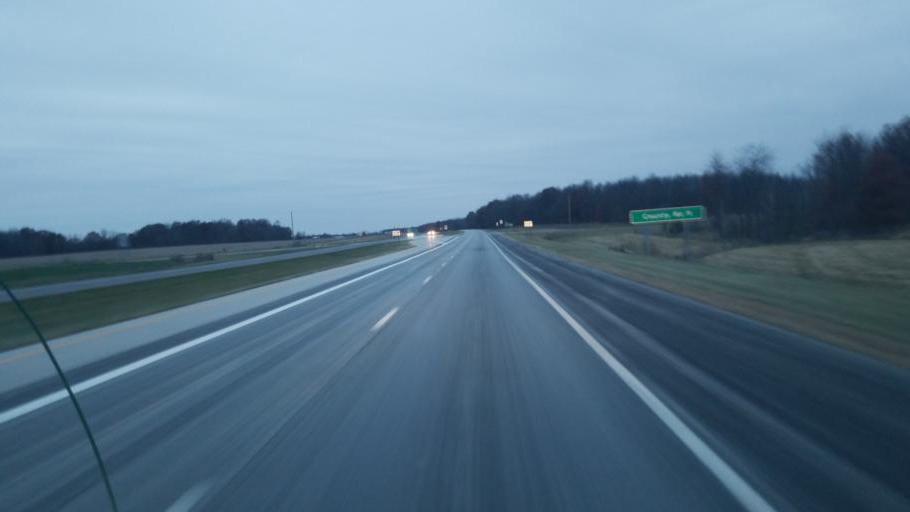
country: US
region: Ohio
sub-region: Hancock County
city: Arlington
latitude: 40.8259
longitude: -83.6967
